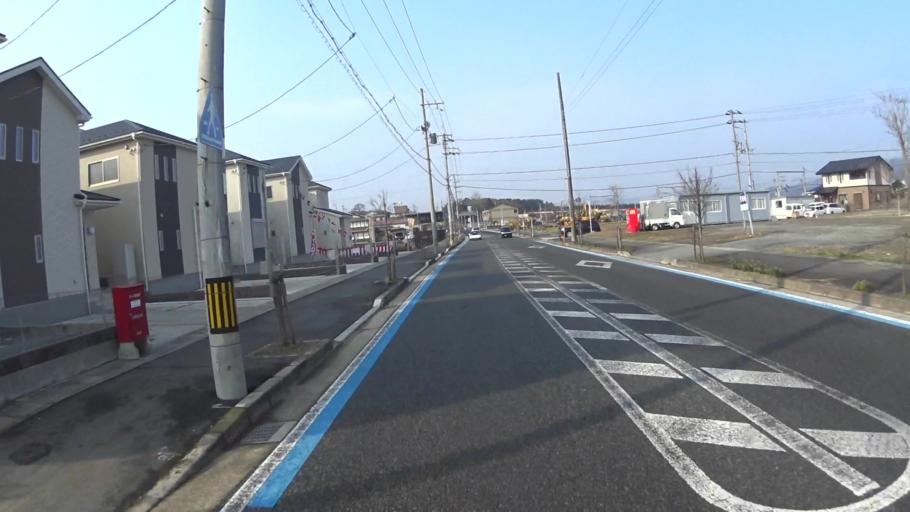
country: JP
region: Kyoto
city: Fukuchiyama
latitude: 35.2988
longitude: 135.1756
